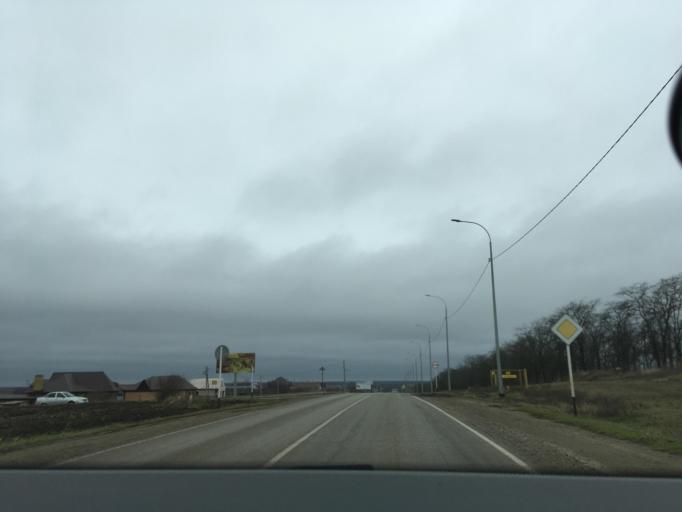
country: RU
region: Krasnodarskiy
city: Kushchevskaya
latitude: 46.5863
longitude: 39.6421
